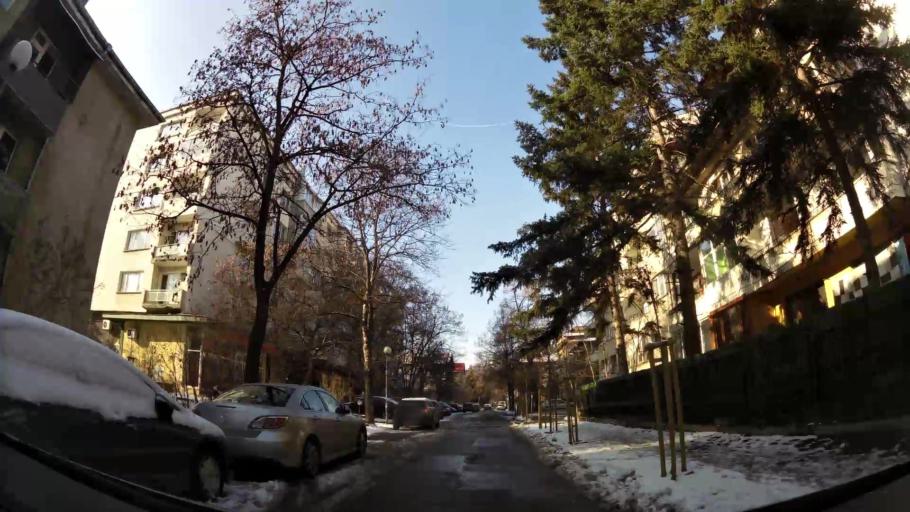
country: BG
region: Sofia-Capital
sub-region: Stolichna Obshtina
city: Sofia
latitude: 42.6699
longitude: 23.3590
